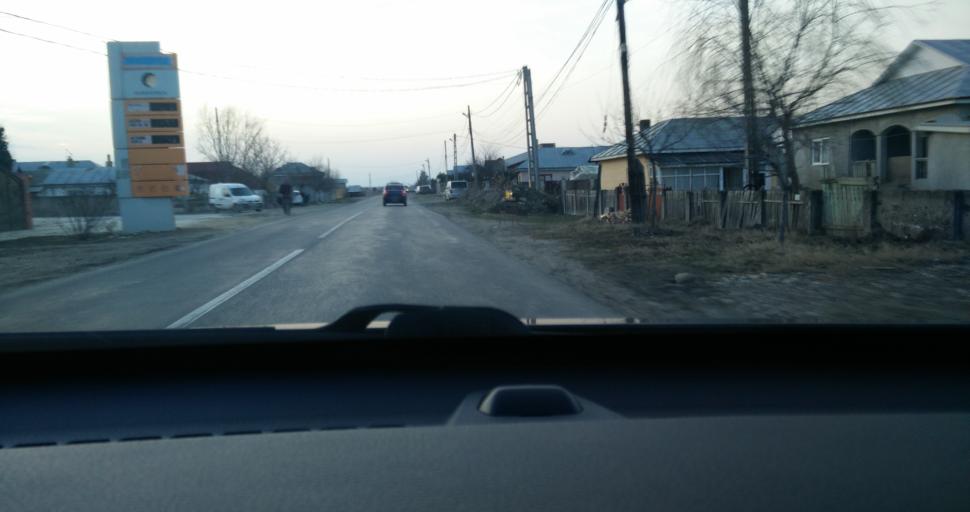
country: RO
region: Vrancea
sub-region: Comuna Rastoaca
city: Rastoaca
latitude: 45.6667
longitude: 27.2679
